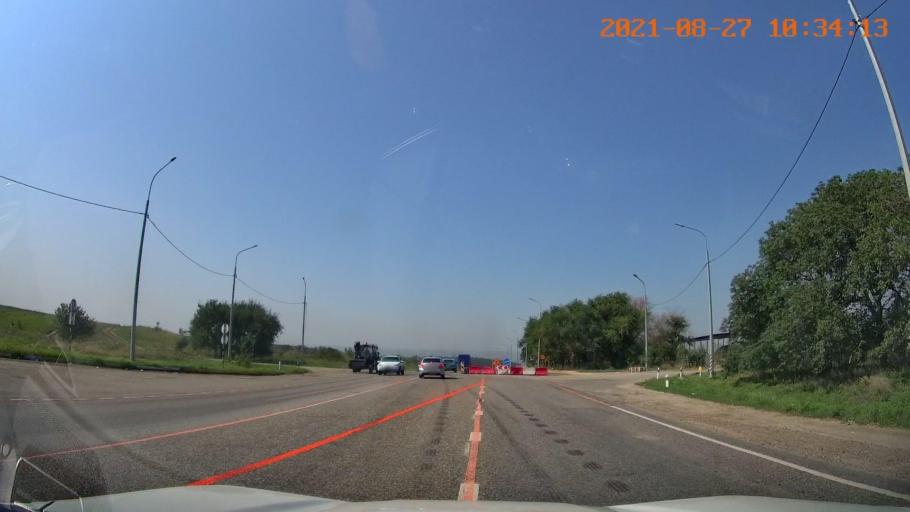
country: RU
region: Karachayevo-Cherkesiya
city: Cherkessk
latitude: 44.2554
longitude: 42.1099
